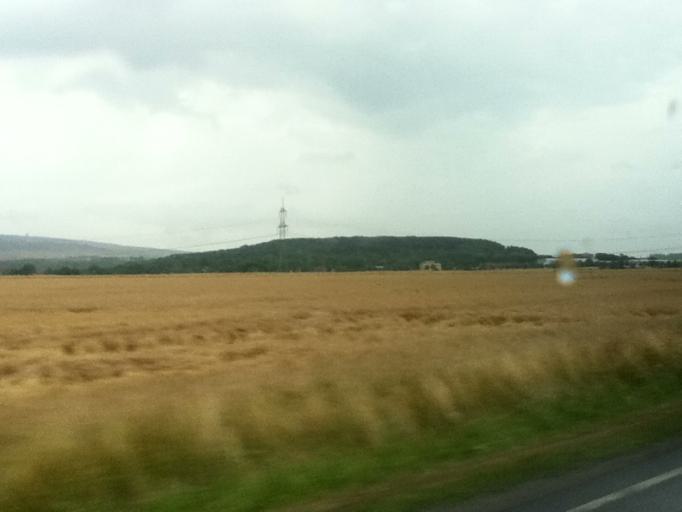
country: DE
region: Thuringia
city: Bechstedtstrass
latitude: 50.9713
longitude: 11.1809
